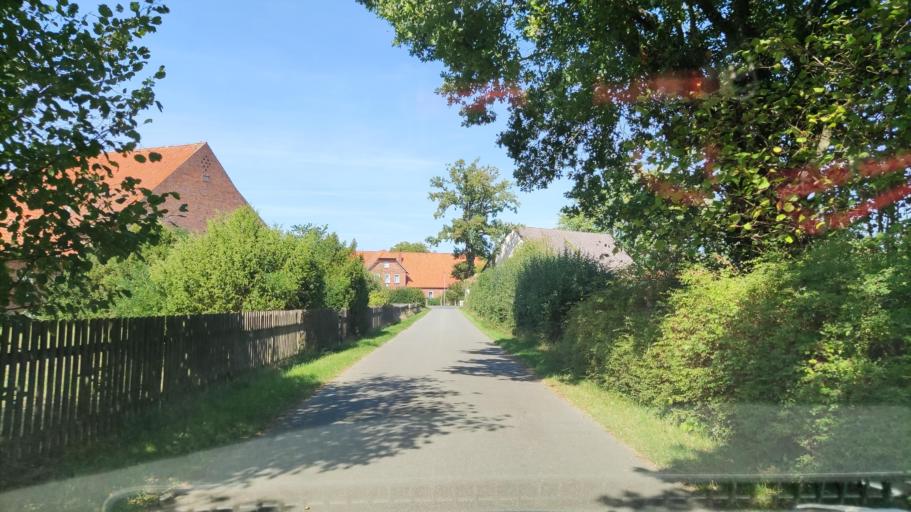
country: DE
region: Lower Saxony
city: Gohrde
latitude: 53.1352
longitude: 10.9539
